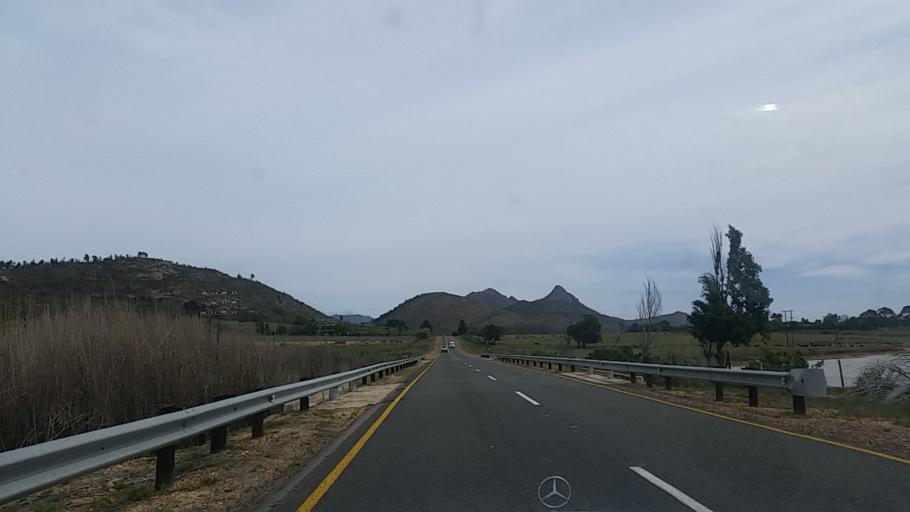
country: ZA
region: Western Cape
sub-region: Eden District Municipality
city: George
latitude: -33.8308
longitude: 22.4607
